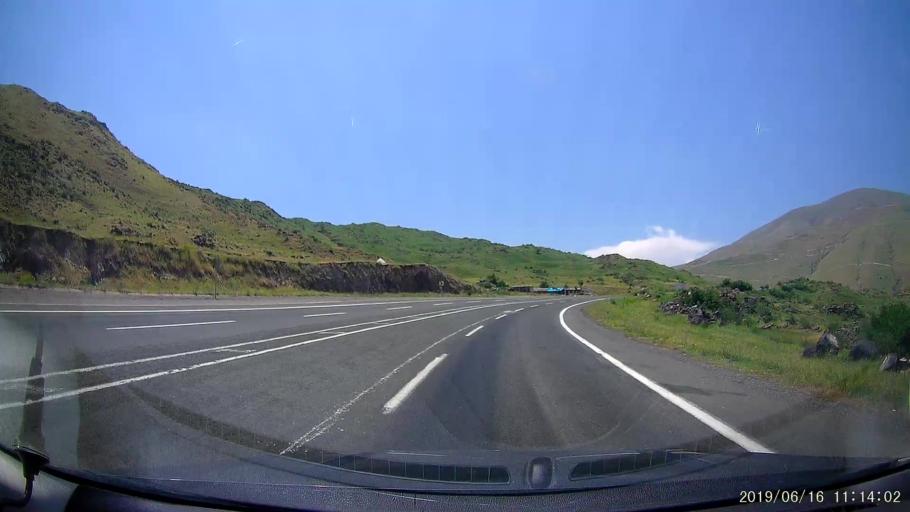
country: TR
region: Igdir
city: Igdir
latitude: 39.7843
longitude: 44.1461
